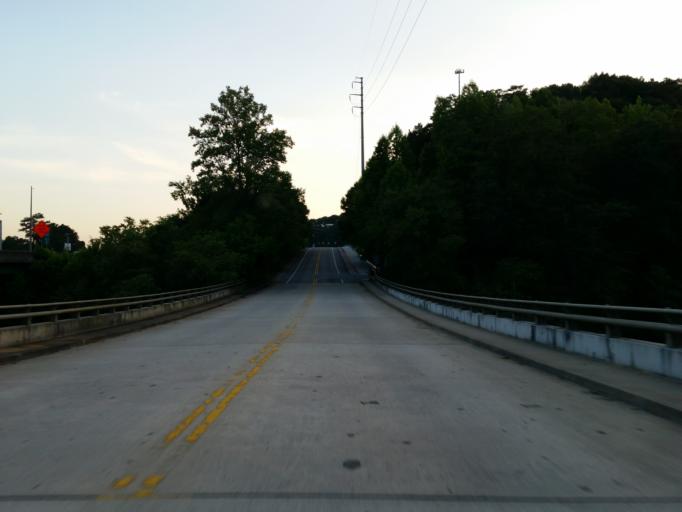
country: US
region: Georgia
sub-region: Cobb County
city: Vinings
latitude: 33.9022
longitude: -84.4429
